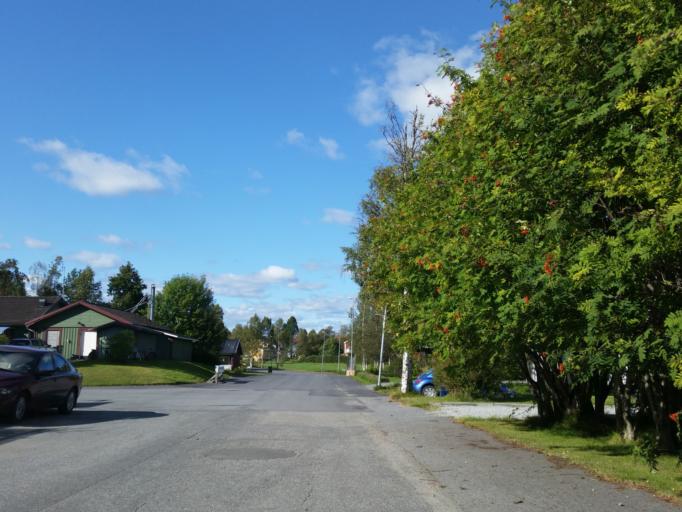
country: SE
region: Vaesterbotten
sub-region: Robertsfors Kommun
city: Robertsfors
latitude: 64.0566
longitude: 20.8572
